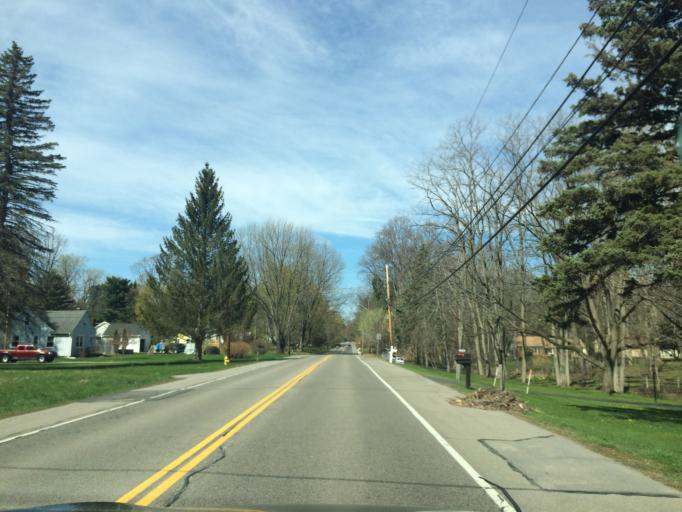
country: US
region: New York
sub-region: Monroe County
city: Fairport
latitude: 43.0790
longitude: -77.4669
